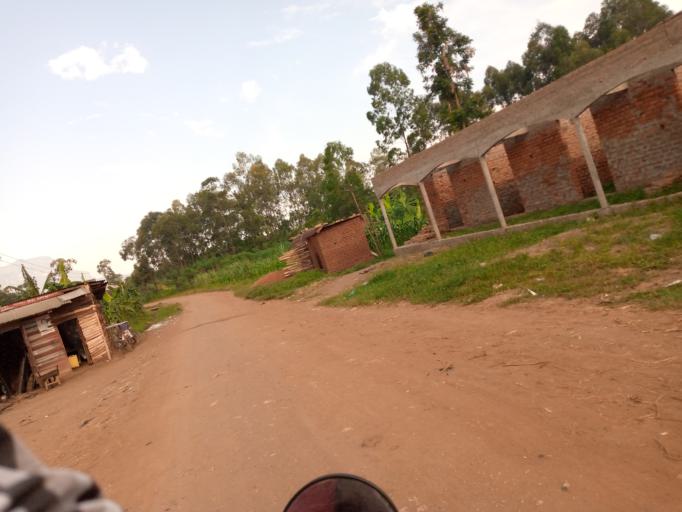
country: UG
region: Eastern Region
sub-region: Mbale District
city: Mbale
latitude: 1.0559
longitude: 34.1617
